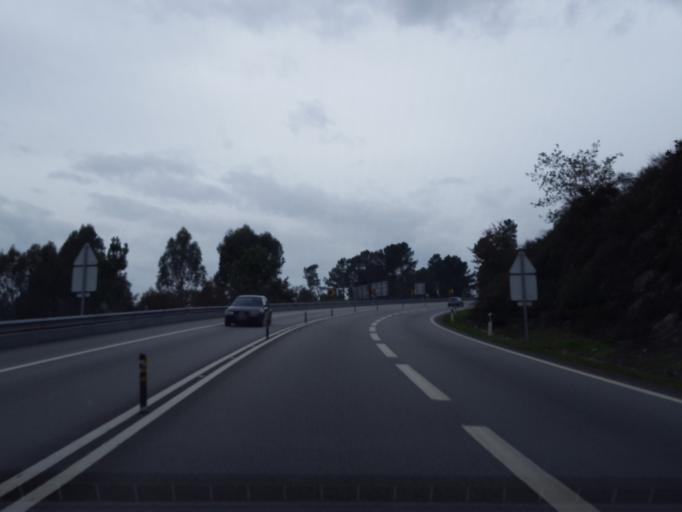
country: PT
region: Porto
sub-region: Marco de Canaveses
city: Marco de Canavezes
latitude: 41.2060
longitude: -8.1643
